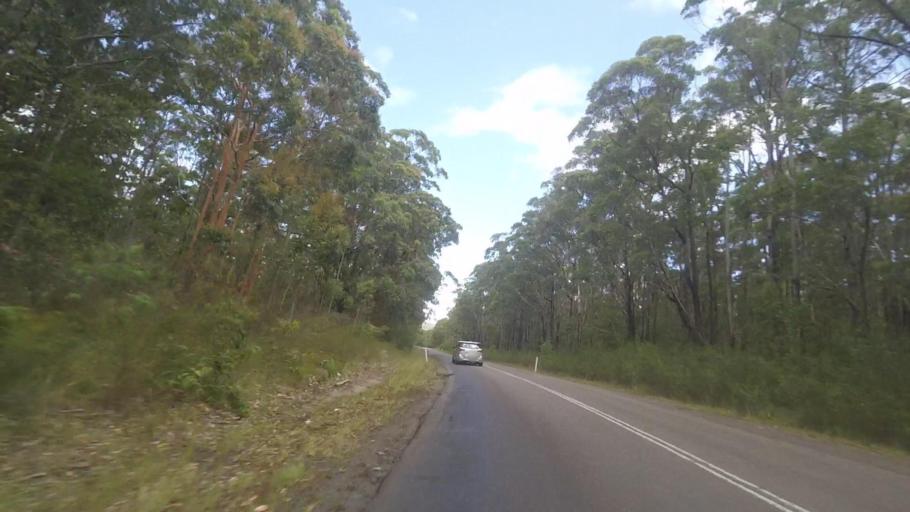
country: AU
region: New South Wales
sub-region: Great Lakes
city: Bulahdelah
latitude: -32.4003
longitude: 152.2570
